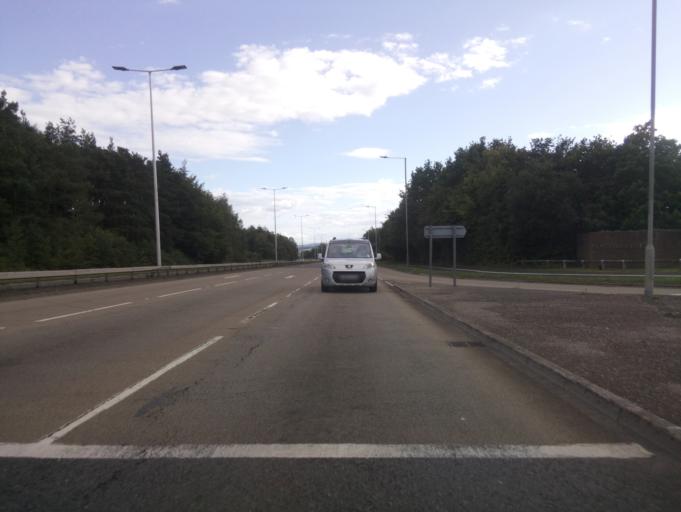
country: GB
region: England
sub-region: Devon
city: Heavitree
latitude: 50.7085
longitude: -3.4852
